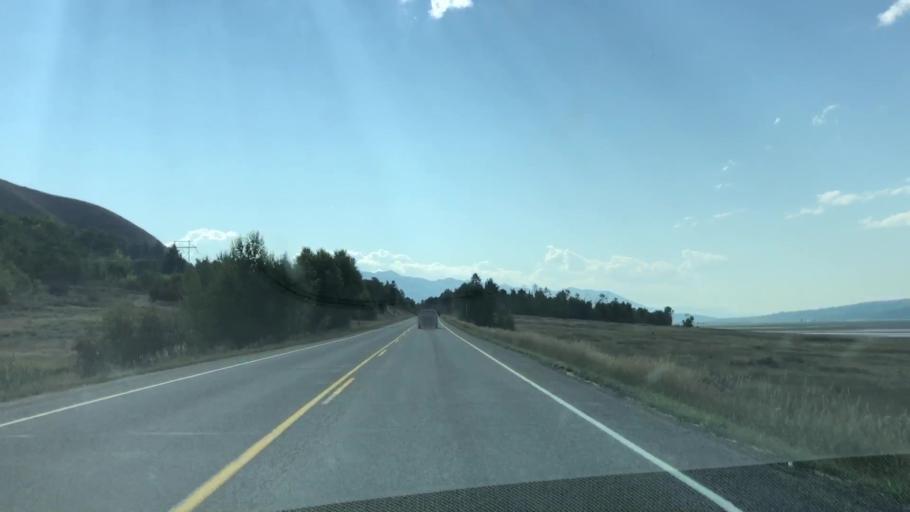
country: US
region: Wyoming
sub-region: Teton County
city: Hoback
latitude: 43.2142
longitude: -111.0621
